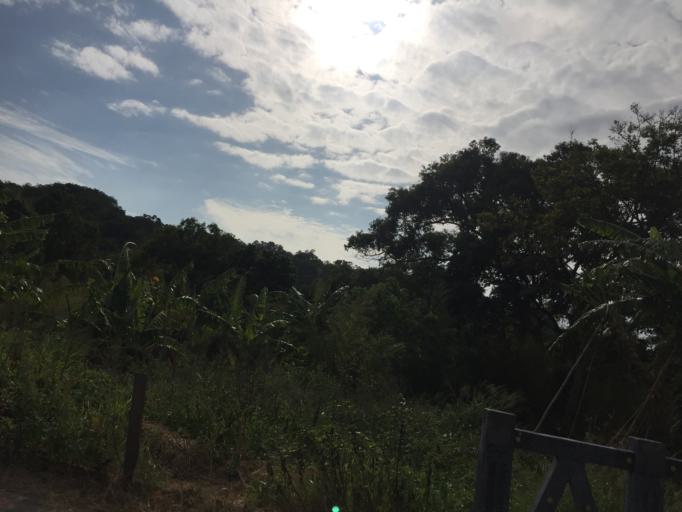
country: TW
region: Taiwan
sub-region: Hsinchu
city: Hsinchu
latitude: 24.7748
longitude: 120.9489
